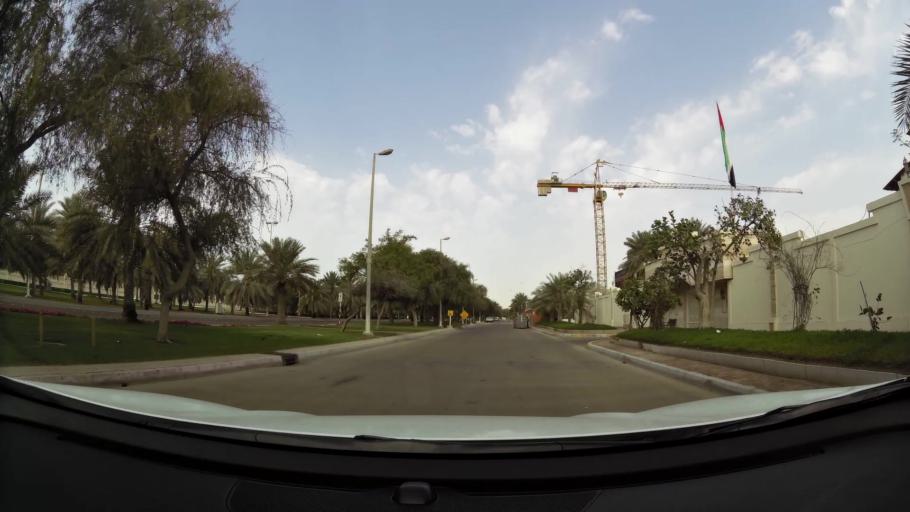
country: AE
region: Abu Dhabi
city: Abu Dhabi
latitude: 24.4374
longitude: 54.3650
